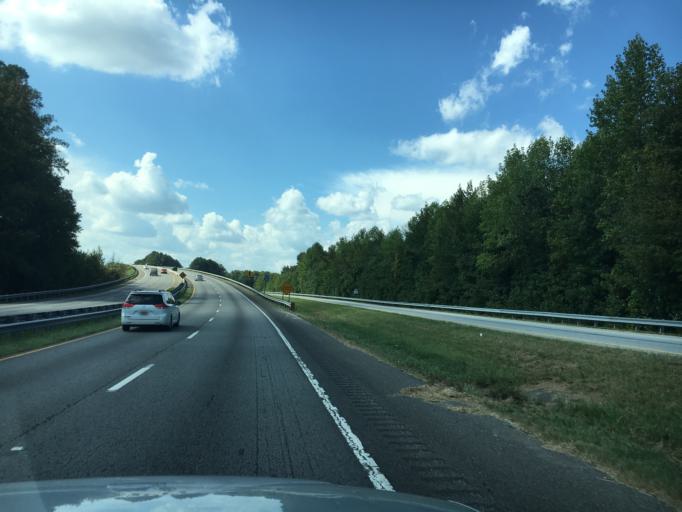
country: US
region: South Carolina
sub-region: Greenville County
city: Fountain Inn
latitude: 34.6665
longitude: -82.1774
